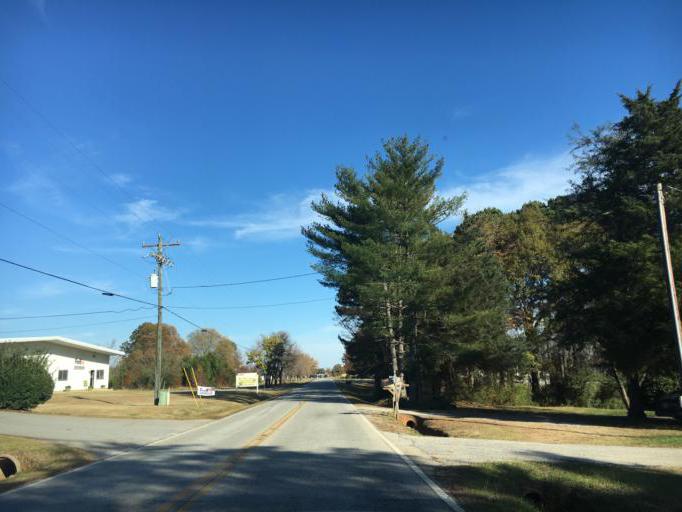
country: US
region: South Carolina
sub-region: Spartanburg County
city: Southern Shops
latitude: 35.0019
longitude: -82.0435
